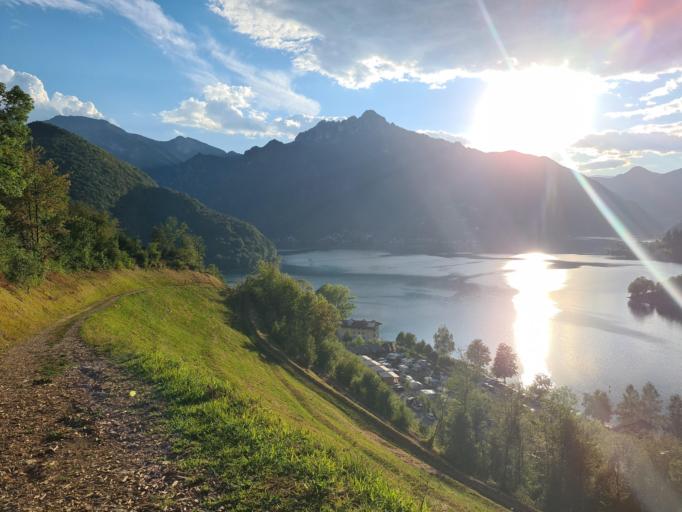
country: IT
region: Trentino-Alto Adige
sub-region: Provincia di Trento
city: Molina di Ledro
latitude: 45.8750
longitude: 10.7698
